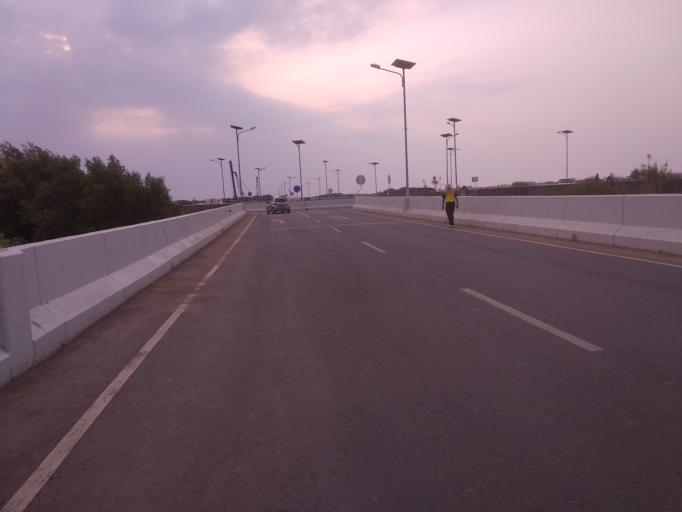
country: ID
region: Central Java
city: Semarang
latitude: -6.9643
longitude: 110.3737
